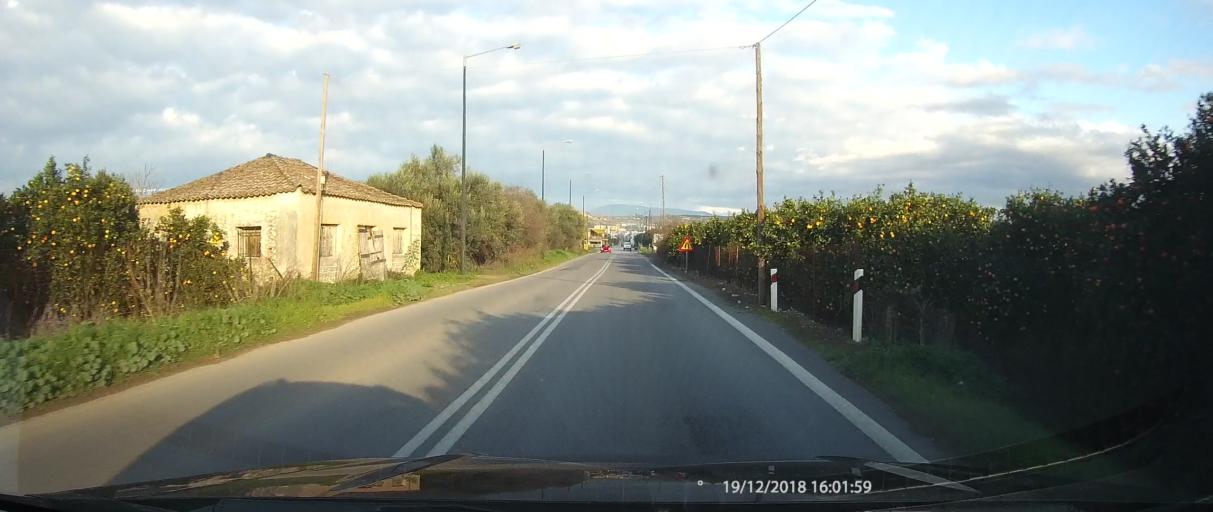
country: GR
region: Peloponnese
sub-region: Nomos Lakonias
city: Vlakhiotis
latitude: 36.8585
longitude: 22.6950
